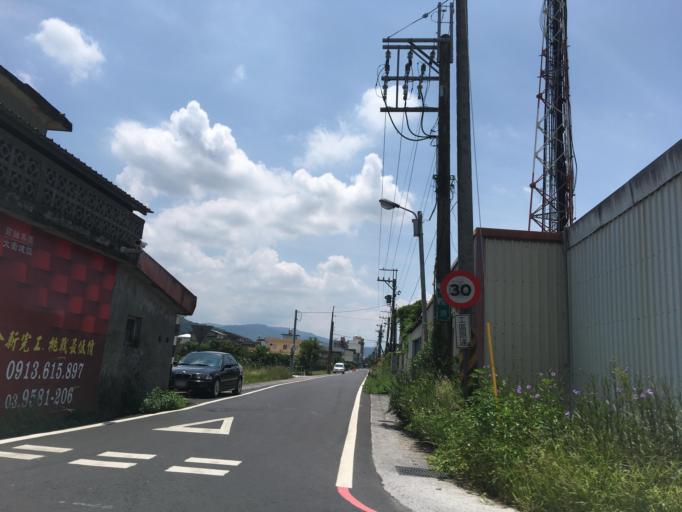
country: TW
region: Taiwan
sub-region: Yilan
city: Yilan
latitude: 24.6521
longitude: 121.7635
